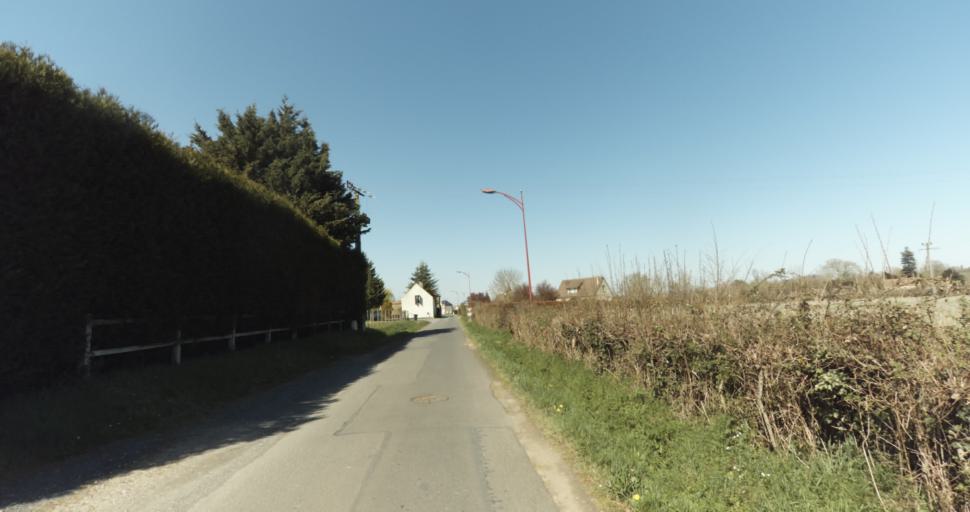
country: FR
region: Lower Normandy
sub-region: Departement du Calvados
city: Saint-Pierre-sur-Dives
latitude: 49.0191
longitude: -0.0087
